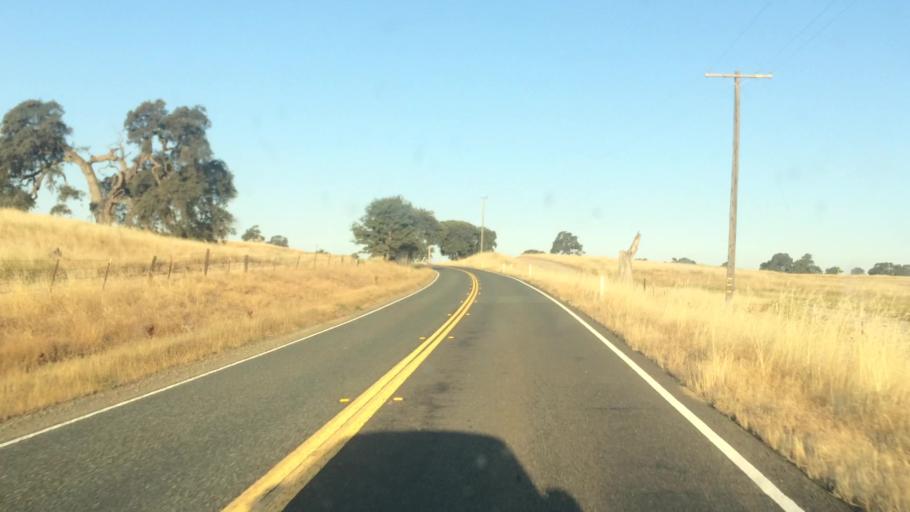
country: US
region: California
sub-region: Amador County
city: Ione
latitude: 38.3614
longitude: -121.0431
